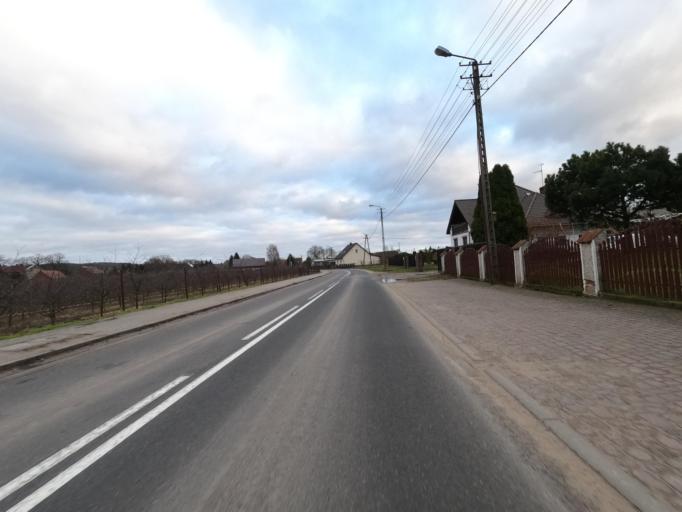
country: PL
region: Greater Poland Voivodeship
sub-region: Powiat pilski
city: Bialosliwie
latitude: 53.1093
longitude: 17.1782
